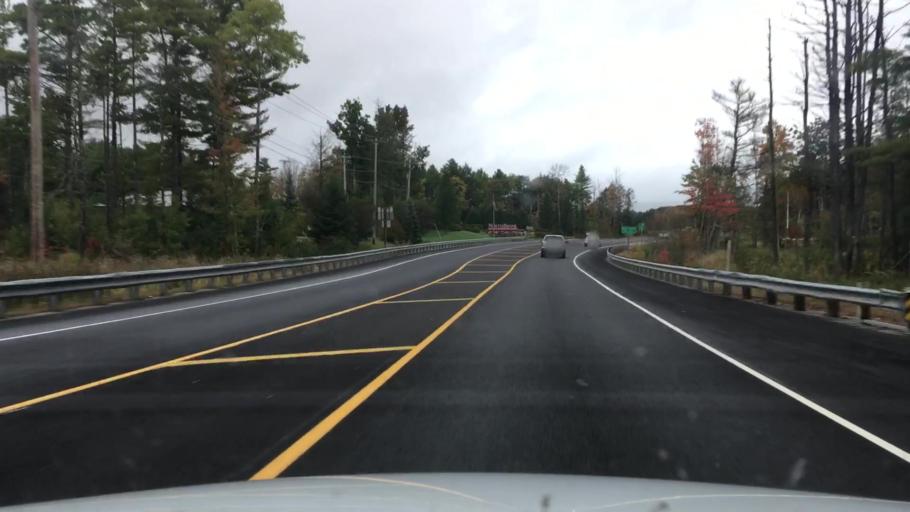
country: US
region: Maine
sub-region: Cumberland County
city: New Gloucester
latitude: 43.8850
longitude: -70.3400
